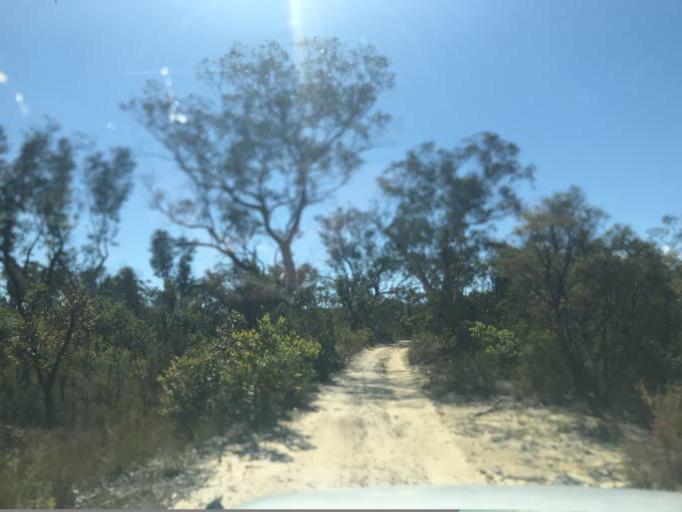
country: AU
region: New South Wales
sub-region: Wyong Shire
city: Little Jilliby
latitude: -33.1540
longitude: 151.1001
